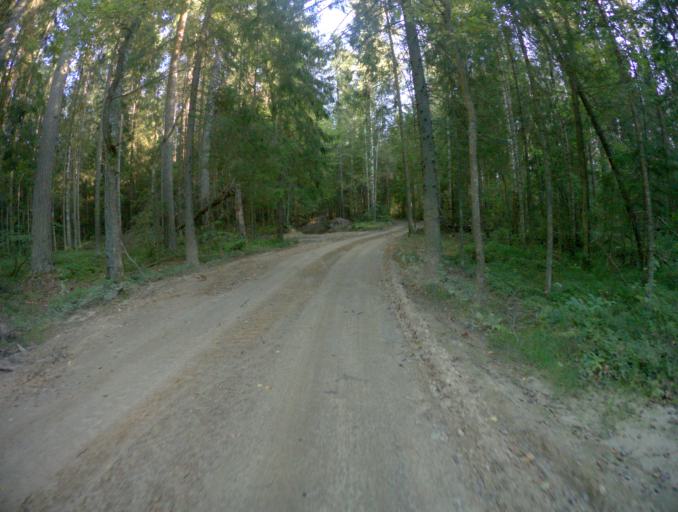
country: RU
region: Vladimir
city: Orgtrud
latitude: 56.1141
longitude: 40.7119
